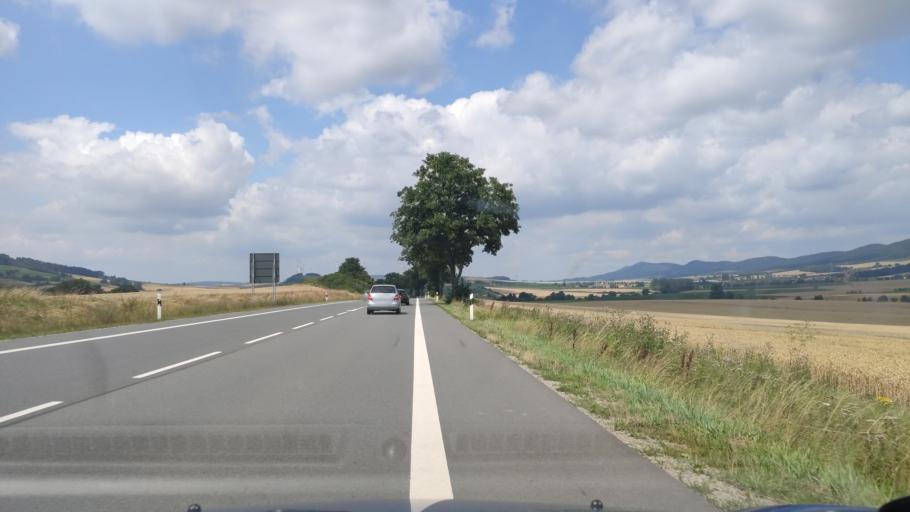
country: DE
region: Lower Saxony
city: Halle
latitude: 51.9816
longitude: 9.5766
